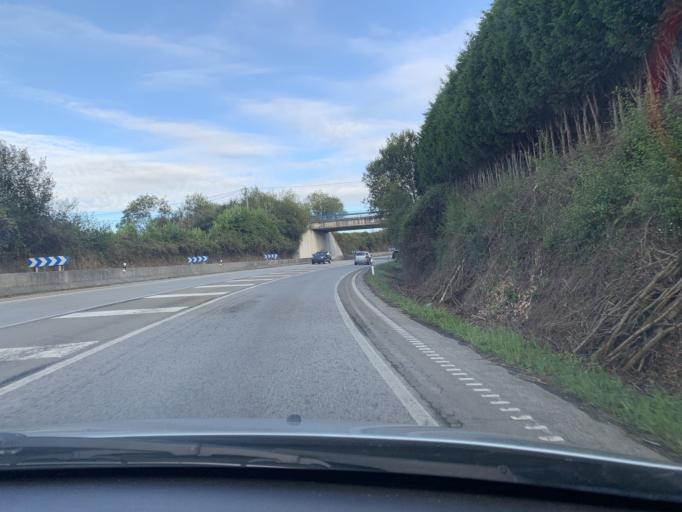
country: ES
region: Galicia
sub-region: Provincia de Lugo
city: Foz
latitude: 43.5544
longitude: -7.2670
